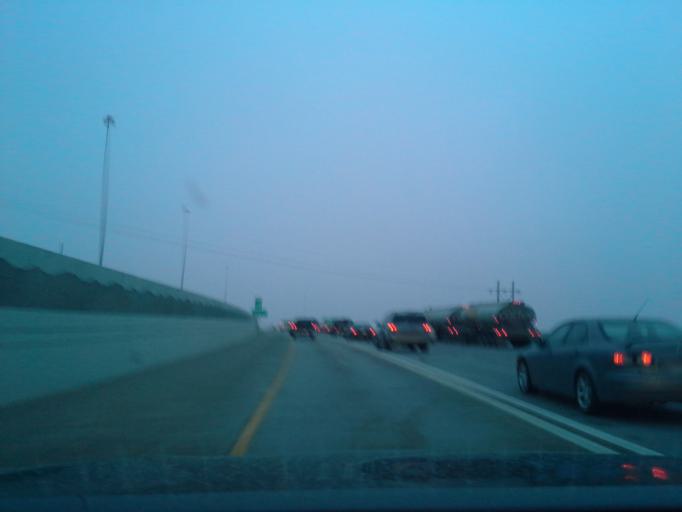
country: US
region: Utah
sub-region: Salt Lake County
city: Midvale
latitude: 40.6326
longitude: -111.9048
